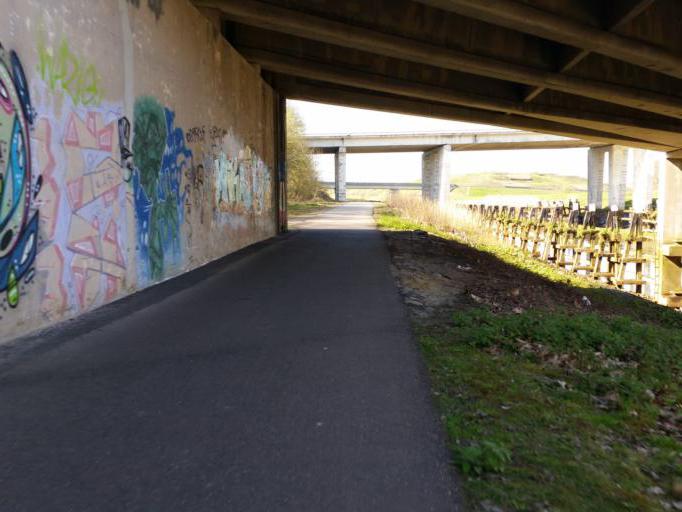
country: BE
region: Flanders
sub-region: Provincie Antwerpen
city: Mechelen
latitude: 51.0414
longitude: 4.4523
